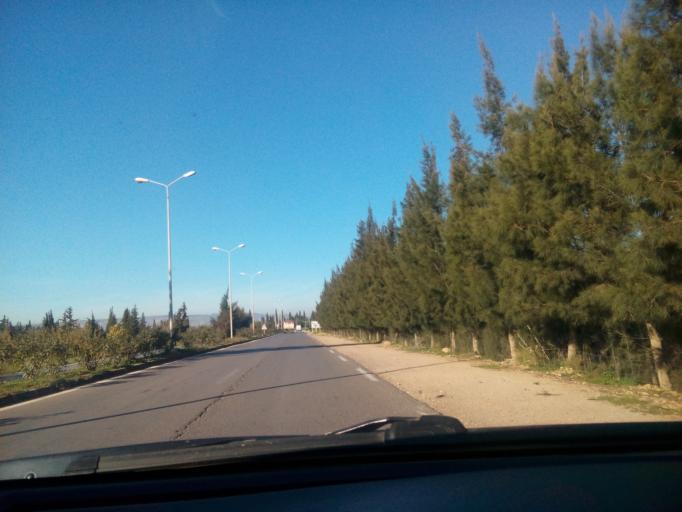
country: DZ
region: Relizane
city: Relizane
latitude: 35.7193
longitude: 0.5076
